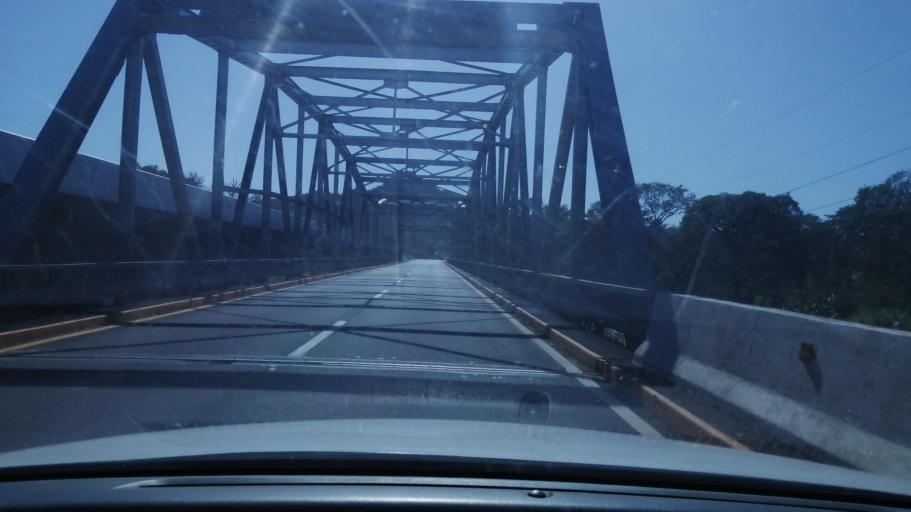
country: PA
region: Chiriqui
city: San Felix
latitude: 8.2797
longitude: -82.0502
